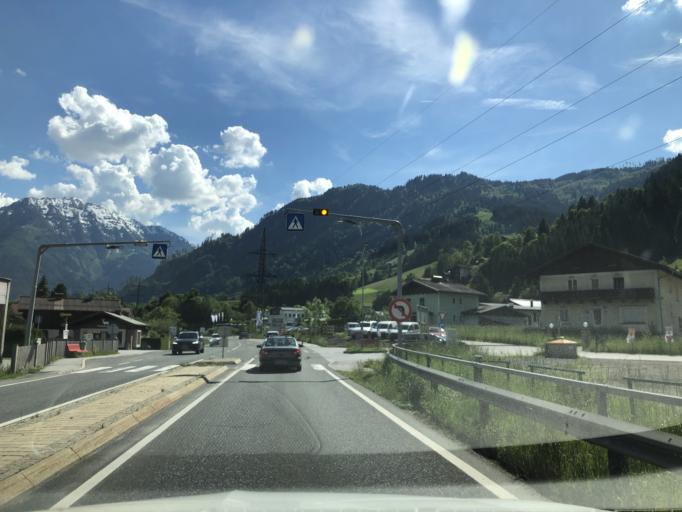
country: AT
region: Salzburg
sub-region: Politischer Bezirk Sankt Johann im Pongau
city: Sankt Johann im Pongau
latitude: 47.3503
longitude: 13.1892
